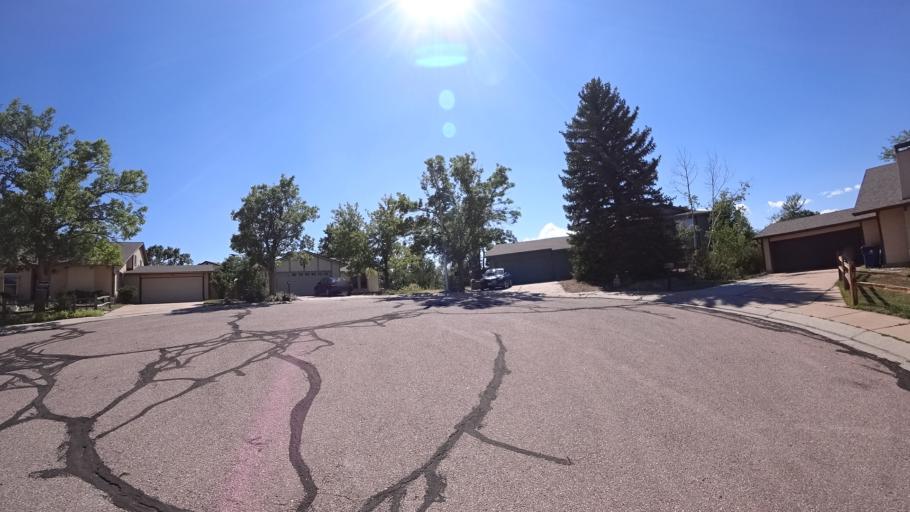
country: US
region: Colorado
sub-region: El Paso County
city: Cimarron Hills
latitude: 38.8766
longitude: -104.7300
